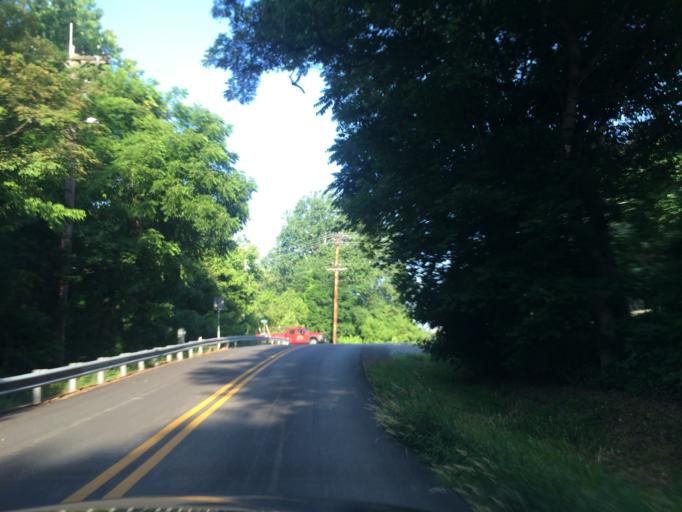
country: US
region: Maryland
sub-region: Carroll County
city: Sykesville
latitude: 39.3530
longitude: -77.0150
